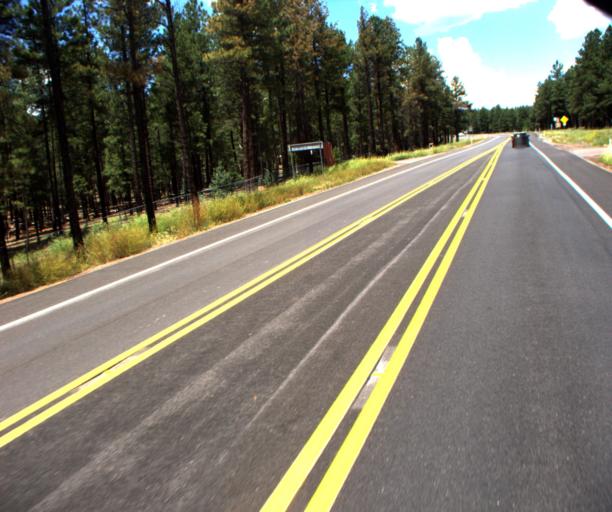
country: US
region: Arizona
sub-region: Coconino County
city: Flagstaff
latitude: 35.2444
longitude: -111.6857
